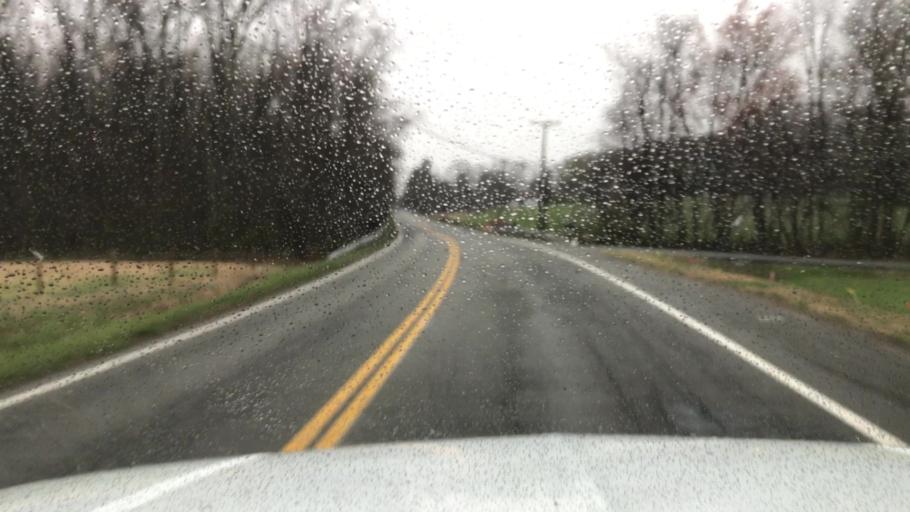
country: US
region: Virginia
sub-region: Henrico County
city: Short Pump
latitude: 37.6611
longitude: -77.6791
